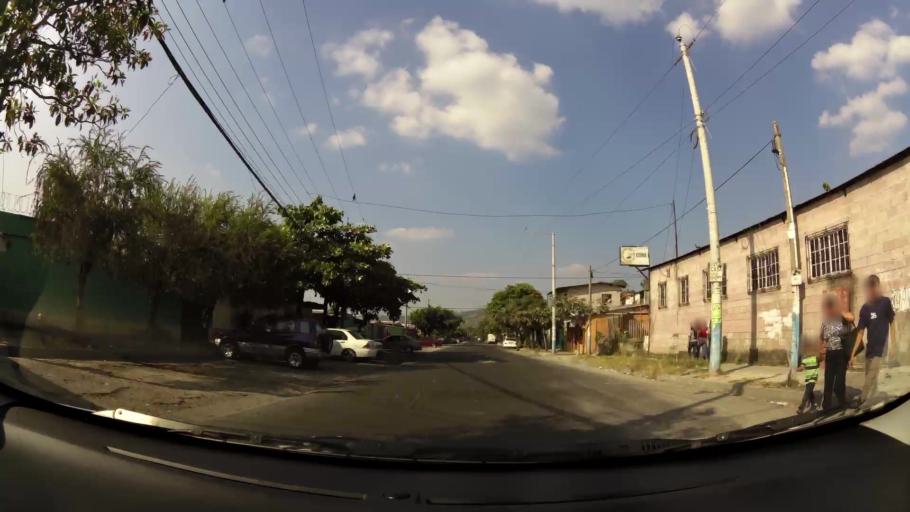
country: SV
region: San Salvador
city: Ilopango
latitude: 13.7182
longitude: -89.1058
